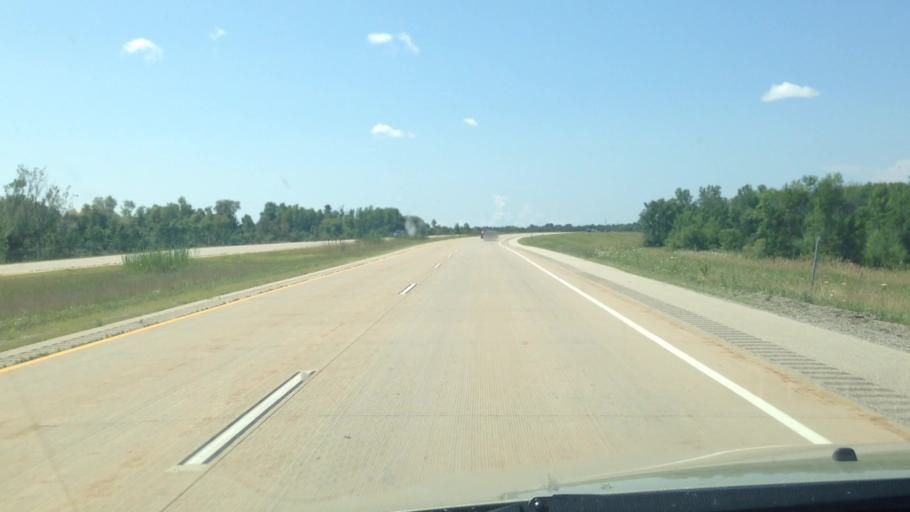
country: US
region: Wisconsin
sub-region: Oconto County
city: Oconto
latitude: 44.9108
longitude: -87.8800
